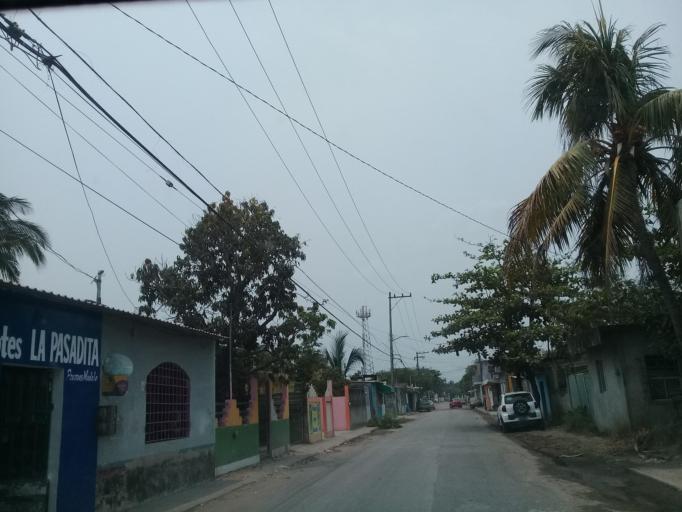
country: MX
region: Veracruz
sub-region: Veracruz
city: Las Amapolas
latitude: 19.1424
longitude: -96.2017
